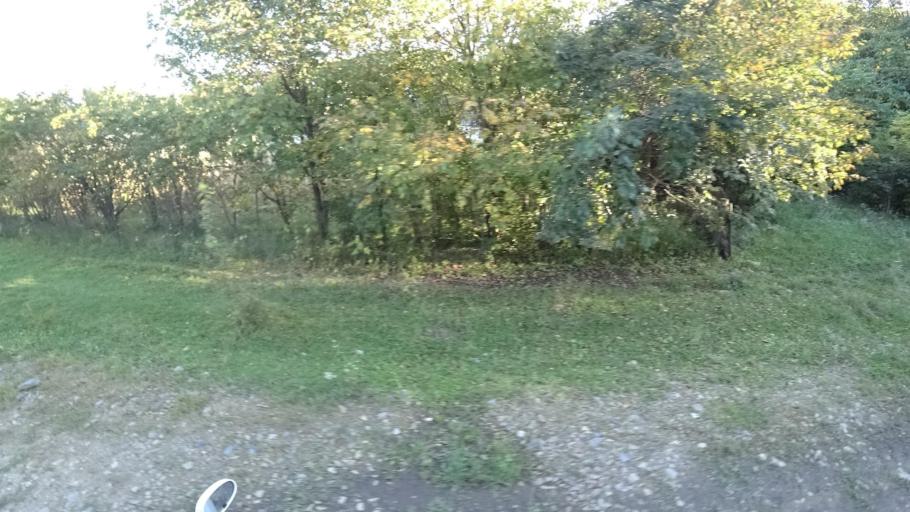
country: RU
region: Primorskiy
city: Kirovskiy
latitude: 44.8291
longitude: 133.5681
